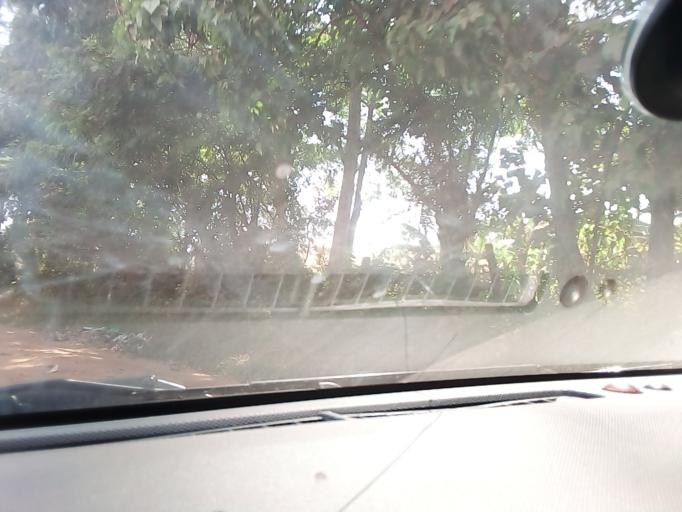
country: UG
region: Central Region
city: Masaka
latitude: -0.3528
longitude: 31.7360
